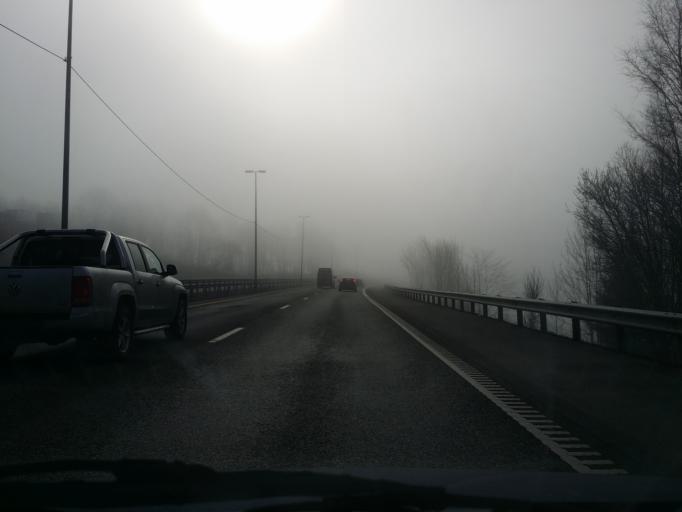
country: NO
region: Buskerud
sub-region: Lier
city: Tranby
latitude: 59.7808
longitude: 10.2753
